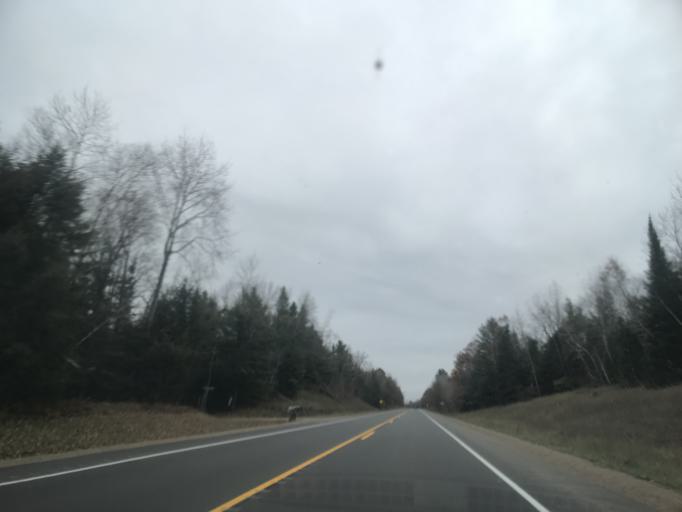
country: US
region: Wisconsin
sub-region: Menominee County
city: Legend Lake
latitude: 45.2660
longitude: -88.5118
